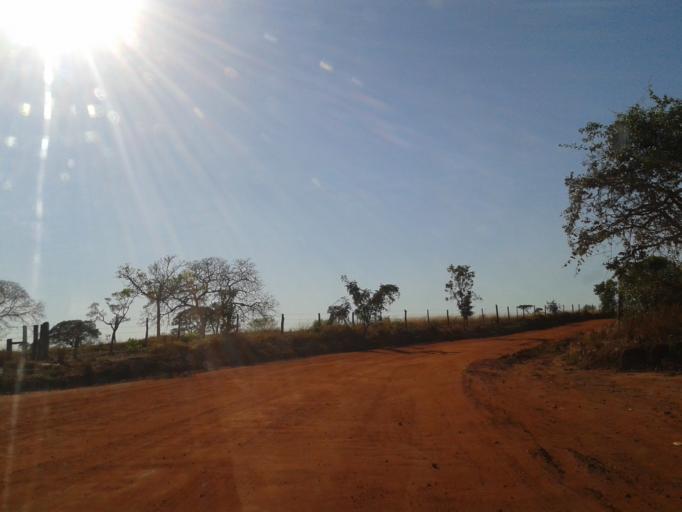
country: BR
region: Minas Gerais
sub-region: Ituiutaba
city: Ituiutaba
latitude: -18.9819
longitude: -49.3987
